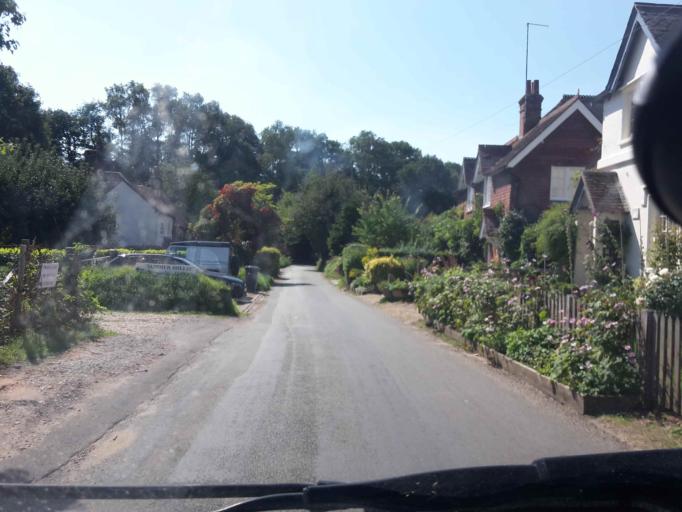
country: GB
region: England
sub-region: Surrey
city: Chilworth
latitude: 51.2088
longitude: -0.4768
